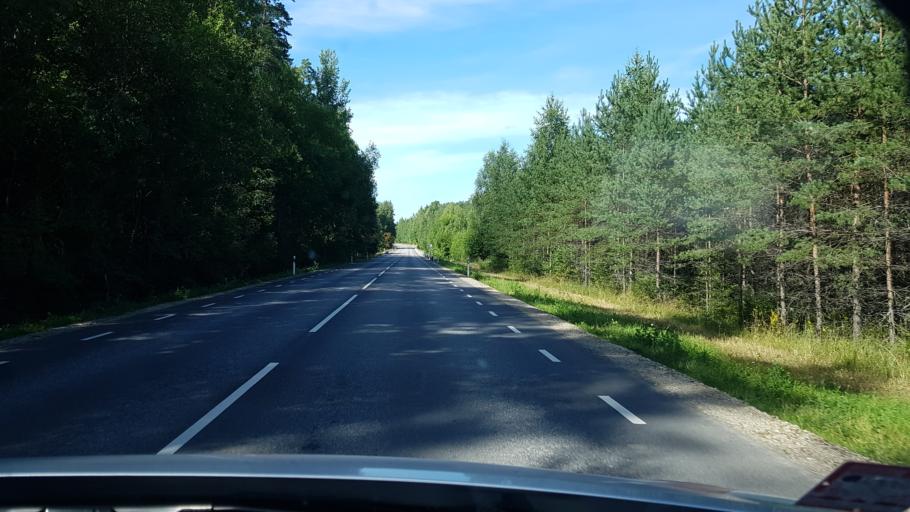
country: EE
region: Polvamaa
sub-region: Polva linn
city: Polva
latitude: 58.0185
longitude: 27.1672
